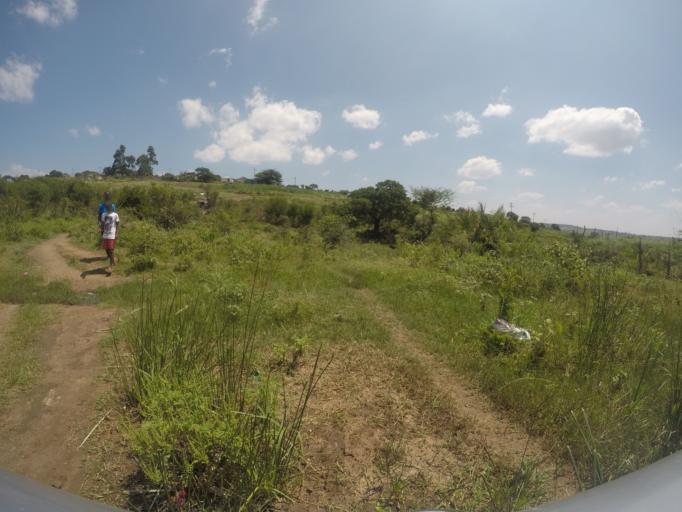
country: ZA
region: KwaZulu-Natal
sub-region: uThungulu District Municipality
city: Empangeni
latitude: -28.6028
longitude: 31.7382
